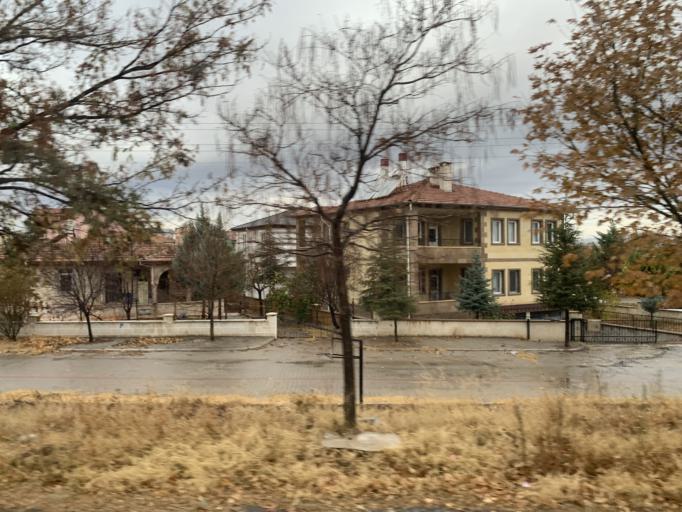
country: TR
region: Nevsehir
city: Avanos
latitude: 38.7092
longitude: 34.8579
